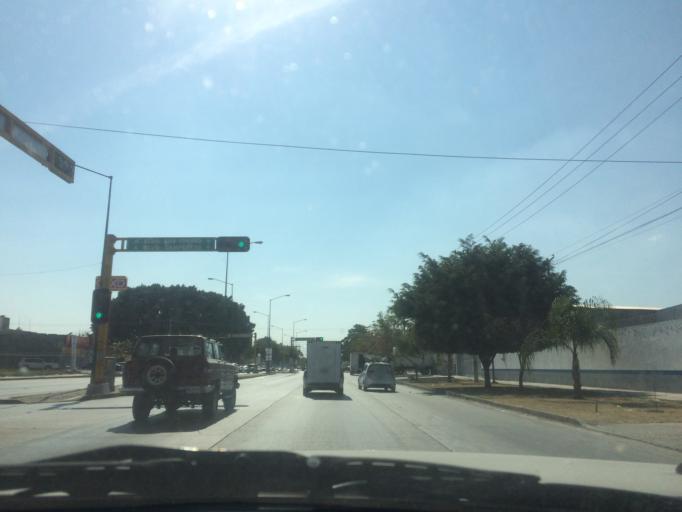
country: MX
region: Guanajuato
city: Leon
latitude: 21.1658
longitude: -101.6626
